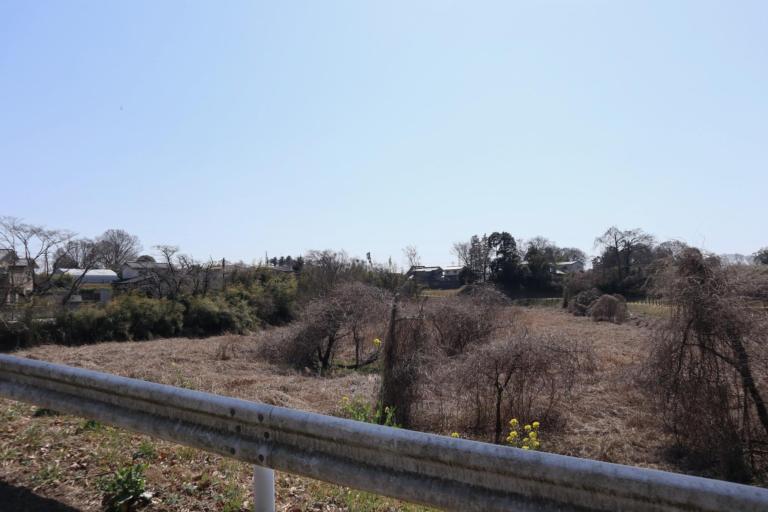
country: JP
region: Ibaraki
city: Koga
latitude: 36.2200
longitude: 139.7108
